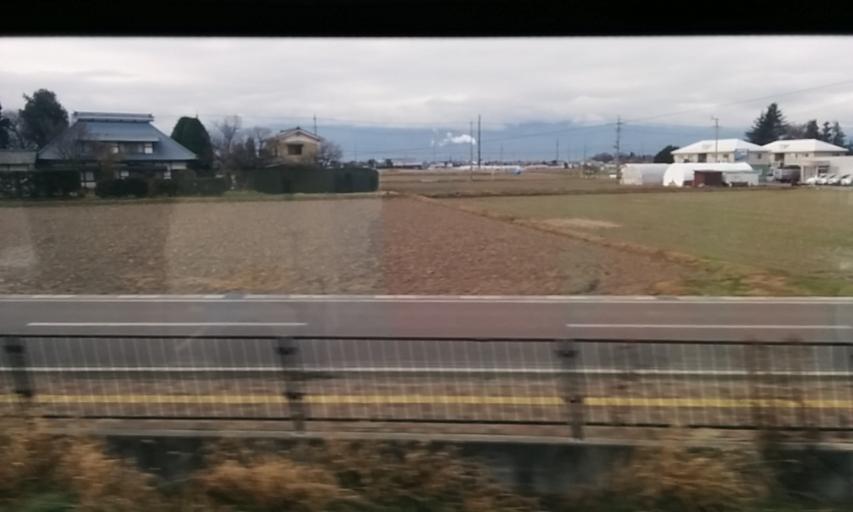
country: JP
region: Nagano
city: Matsumoto
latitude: 36.1930
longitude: 137.9631
